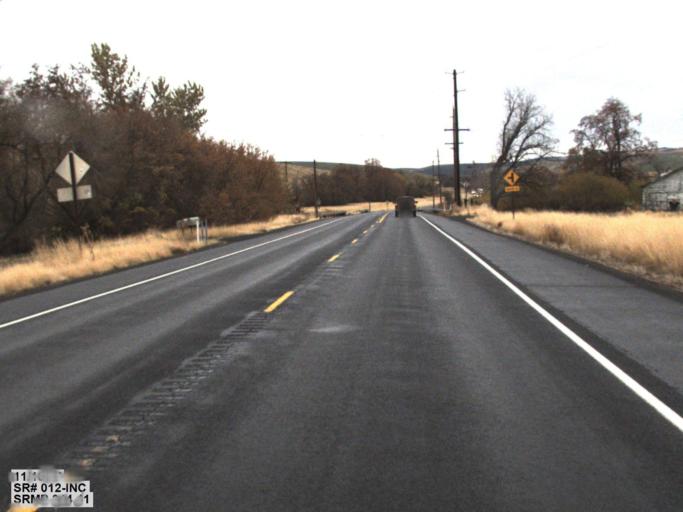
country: US
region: Washington
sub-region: Walla Walla County
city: Walla Walla East
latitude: 46.1179
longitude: -118.2176
